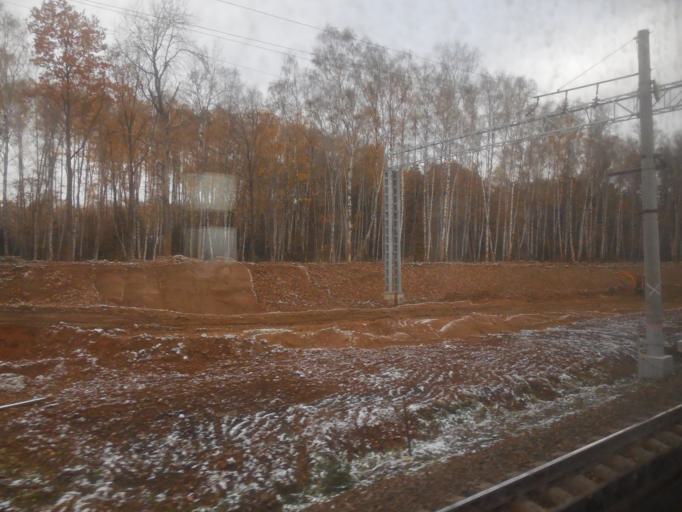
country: RU
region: Moskovskaya
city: Novoivanovskoye
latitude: 55.7013
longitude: 37.3443
